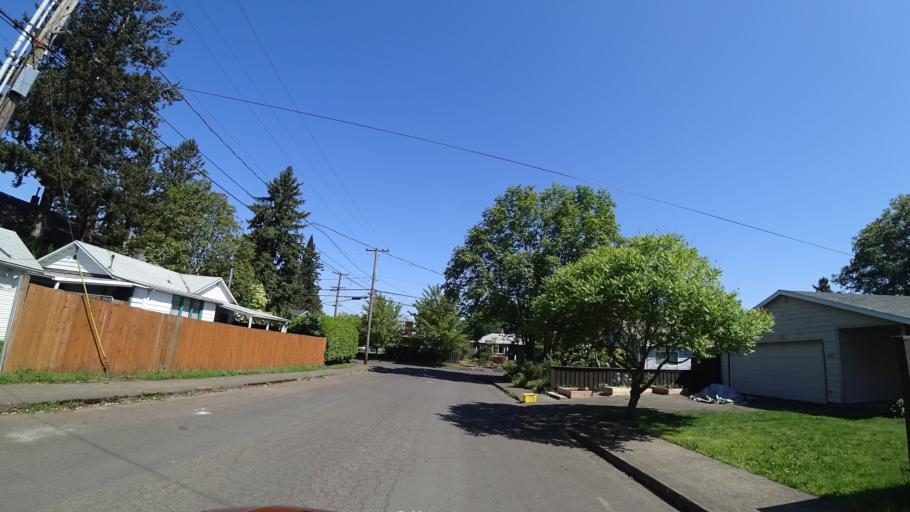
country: US
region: Oregon
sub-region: Multnomah County
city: Lents
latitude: 45.4931
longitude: -122.6129
